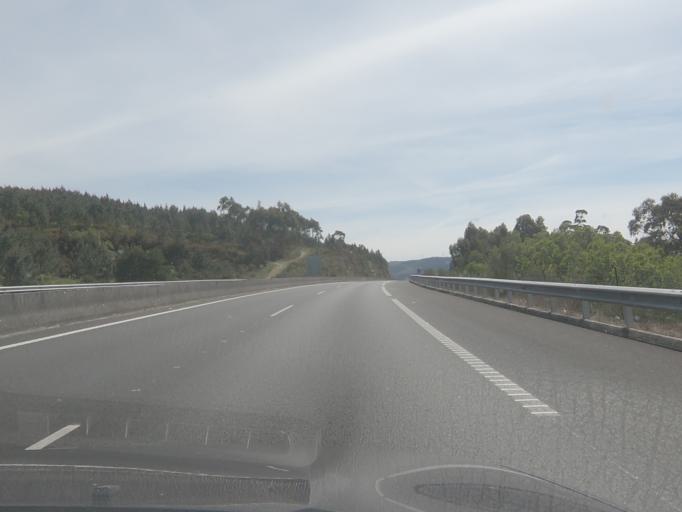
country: ES
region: Galicia
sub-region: Provincia de Pontevedra
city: Valga
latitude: 42.7203
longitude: -8.6414
